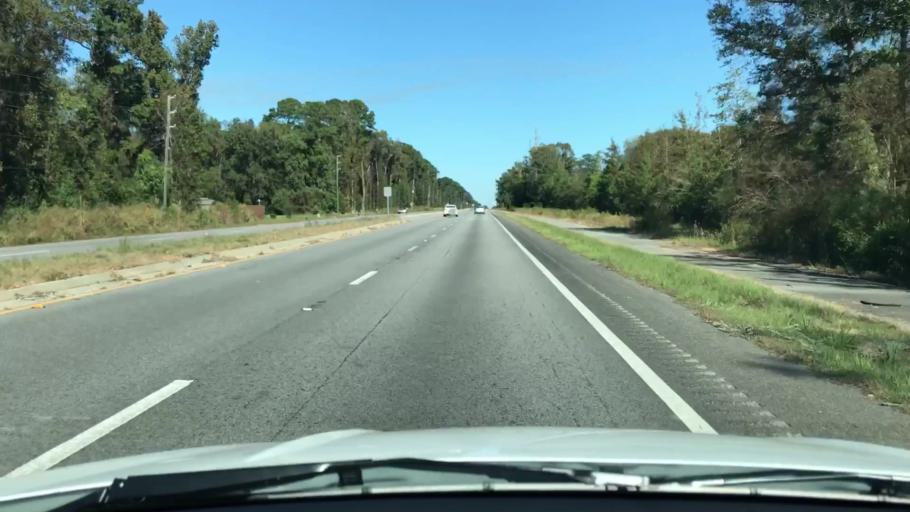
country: US
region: South Carolina
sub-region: Hampton County
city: Yemassee
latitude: 32.6061
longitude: -80.7537
